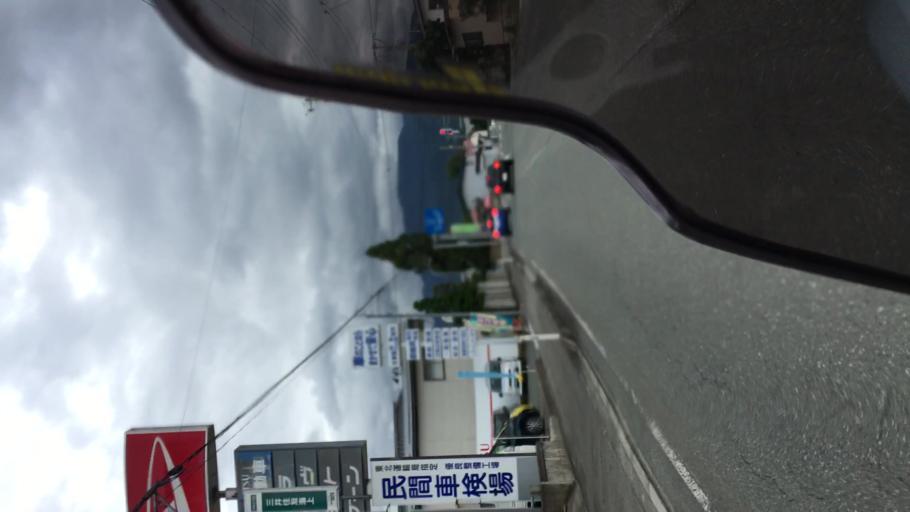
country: JP
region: Yamagata
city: Tendo
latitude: 38.3275
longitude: 140.3963
